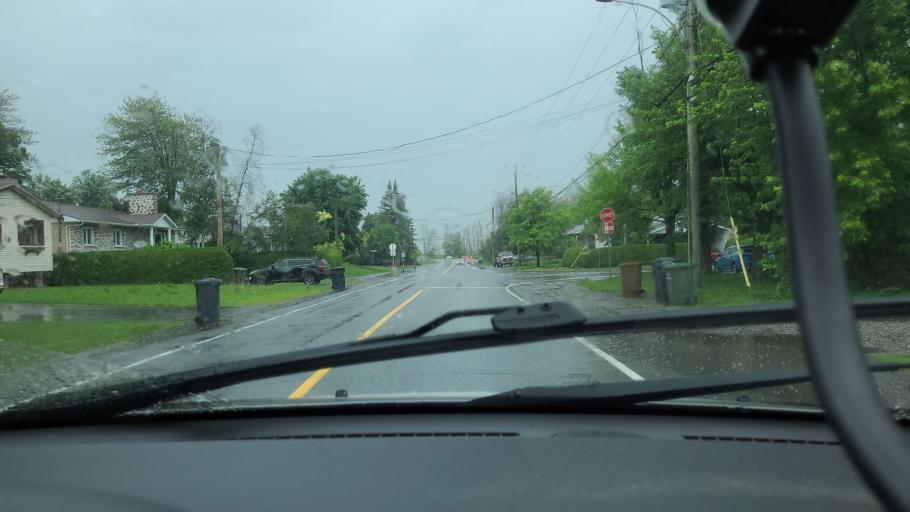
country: CA
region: Quebec
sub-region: Monteregie
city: Saint-Hyacinthe
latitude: 45.6156
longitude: -72.9836
